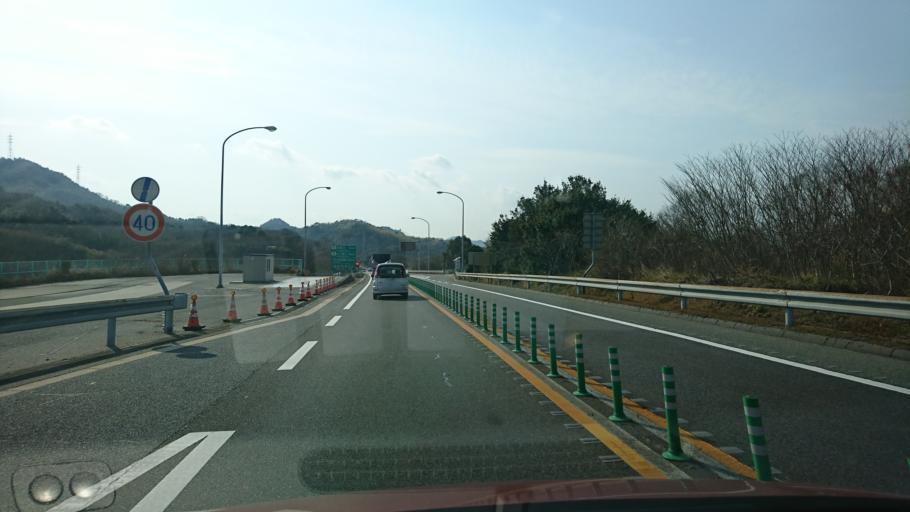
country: JP
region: Hiroshima
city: Onomichi
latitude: 34.3779
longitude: 133.1921
